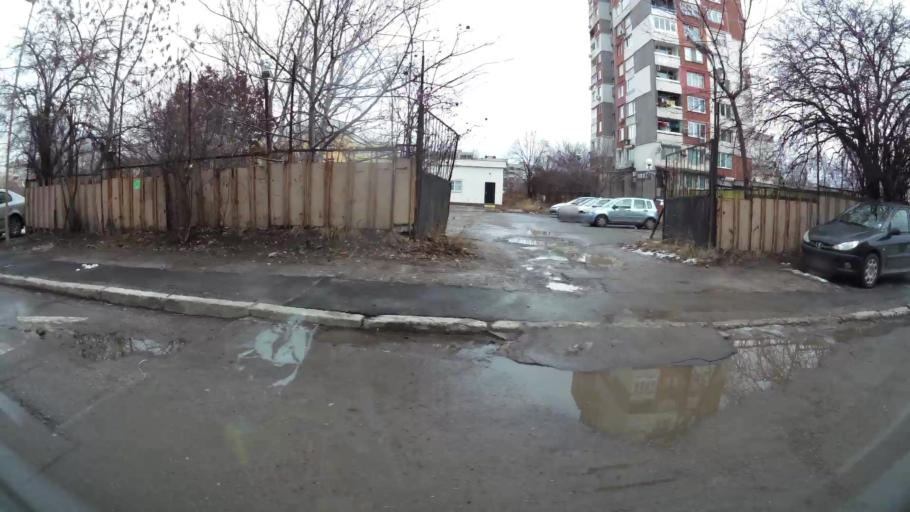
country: BG
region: Sofiya
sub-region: Obshtina Bozhurishte
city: Bozhurishte
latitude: 42.7239
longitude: 23.2523
